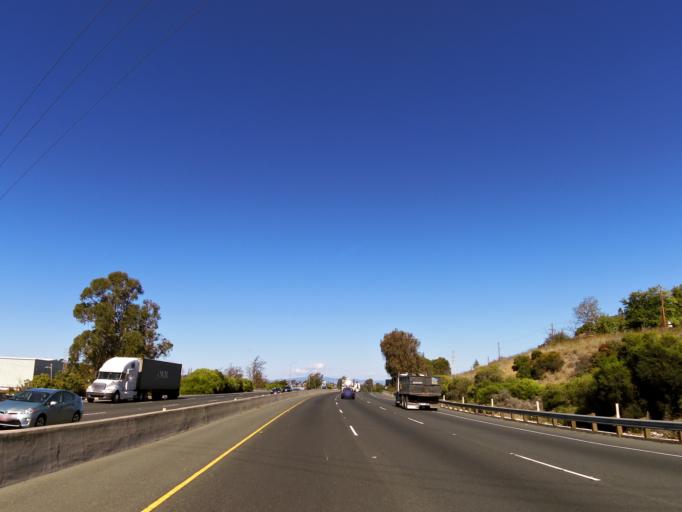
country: US
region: California
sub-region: Contra Costa County
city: Crockett
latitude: 38.0752
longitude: -122.2308
